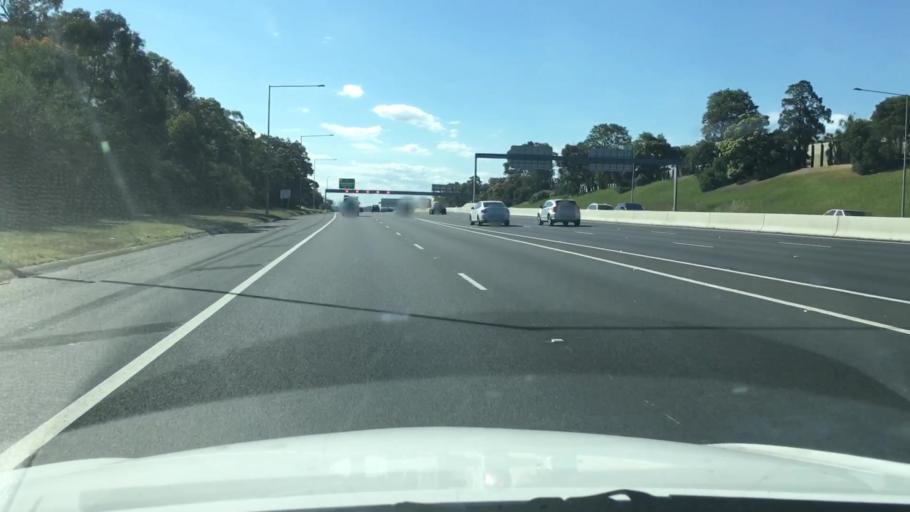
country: AU
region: Victoria
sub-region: Casey
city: Eumemmerring
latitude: -37.9863
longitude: 145.2494
